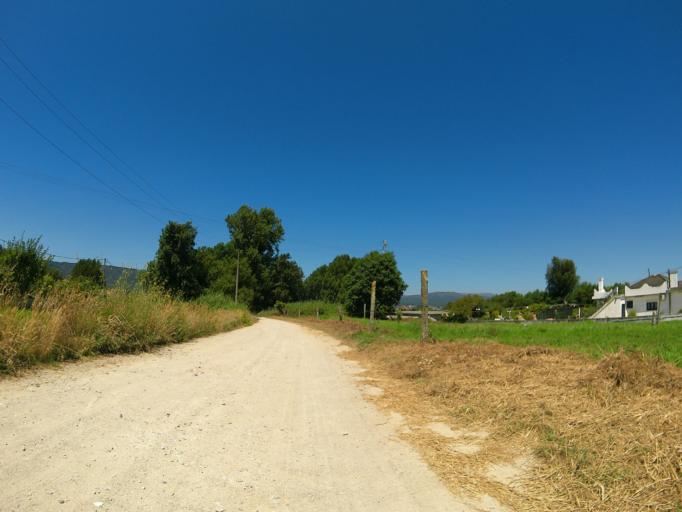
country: PT
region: Viana do Castelo
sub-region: Viana do Castelo
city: Meadela
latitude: 41.6871
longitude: -8.8042
